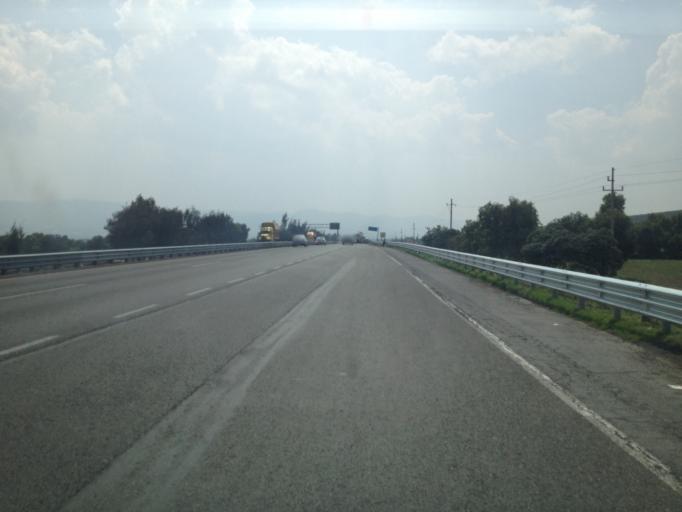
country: MX
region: Puebla
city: Cuacnopalan
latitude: 18.8281
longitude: -97.4947
